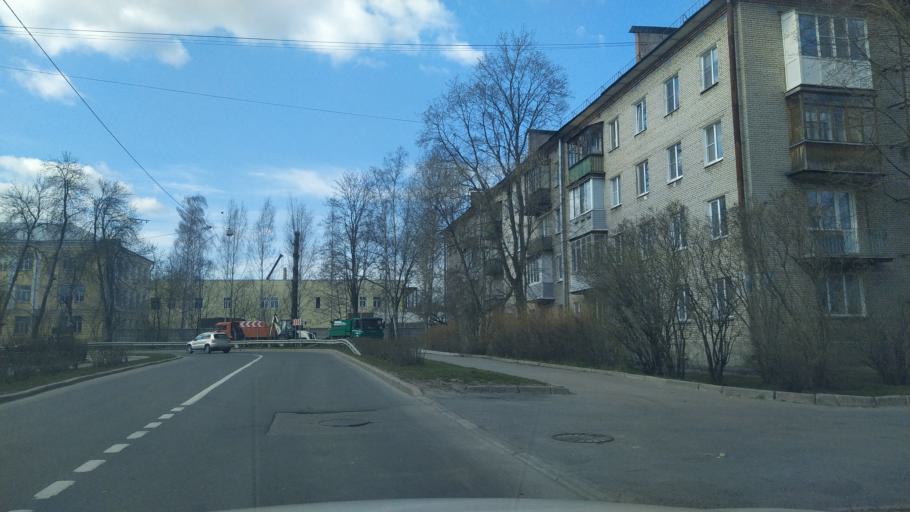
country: RU
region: St.-Petersburg
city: Pushkin
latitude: 59.7034
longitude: 30.4143
